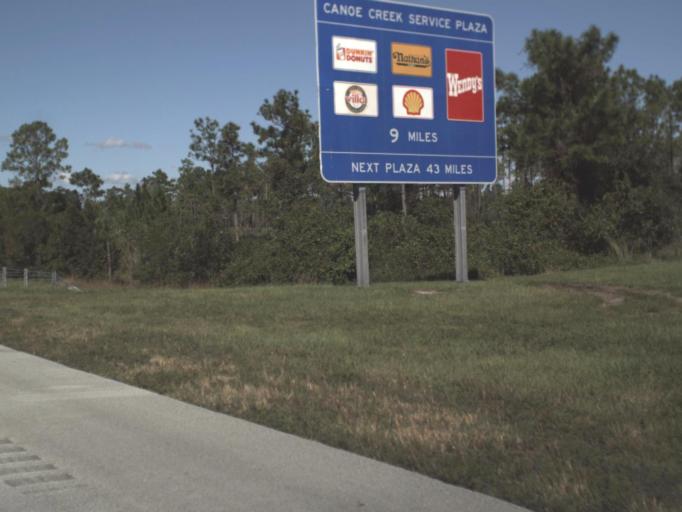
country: US
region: Florida
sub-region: Osceola County
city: Saint Cloud
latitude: 28.0057
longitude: -81.1504
